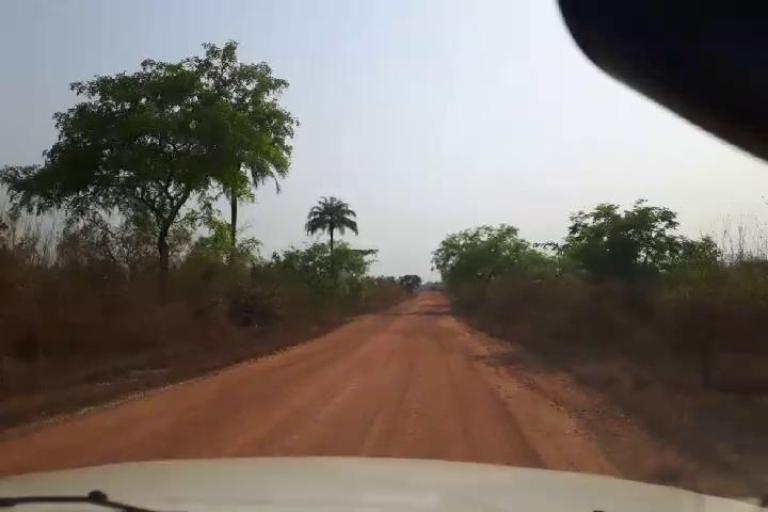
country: SL
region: Northern Province
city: Masingbi
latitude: 8.8019
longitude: -11.8642
